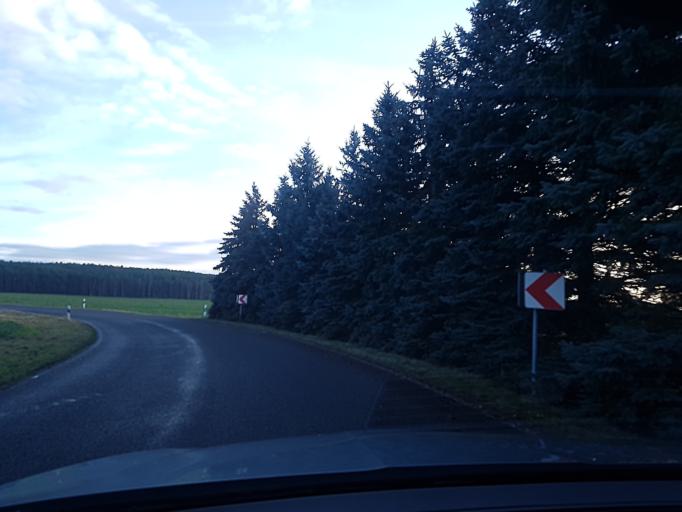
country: DE
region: Brandenburg
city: Trobitz
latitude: 51.5719
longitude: 13.4124
